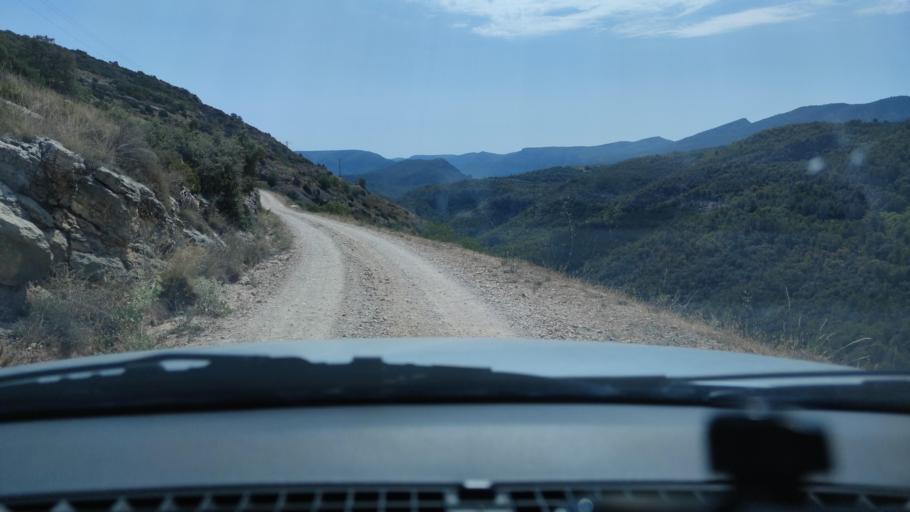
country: ES
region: Catalonia
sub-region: Provincia de Lleida
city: Ager
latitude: 41.9278
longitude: 0.8083
